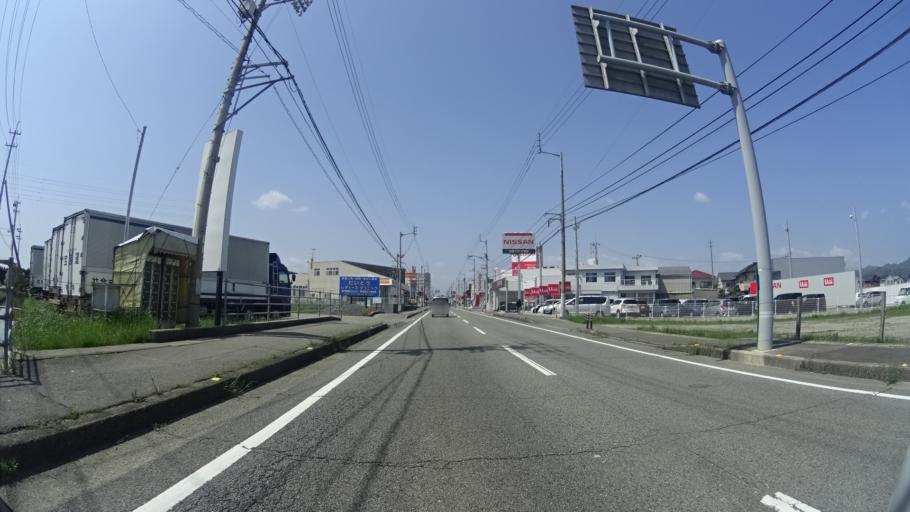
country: JP
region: Tokushima
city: Narutocho-mitsuishi
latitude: 34.1648
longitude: 134.5973
